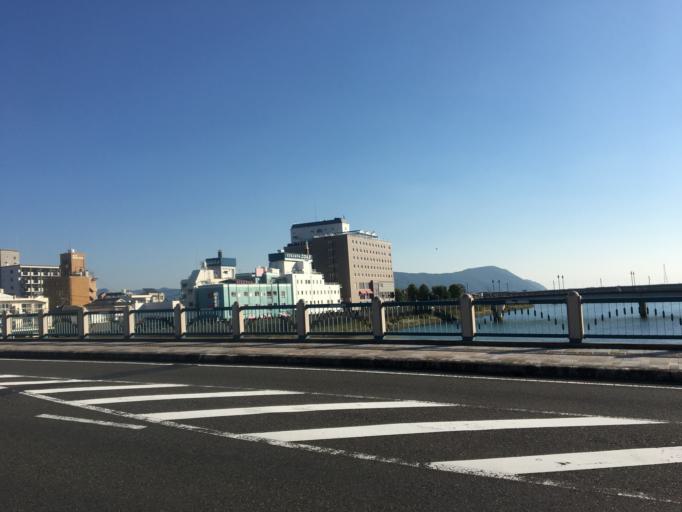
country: JP
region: Miyazaki
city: Nobeoka
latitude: 32.5832
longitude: 131.6687
